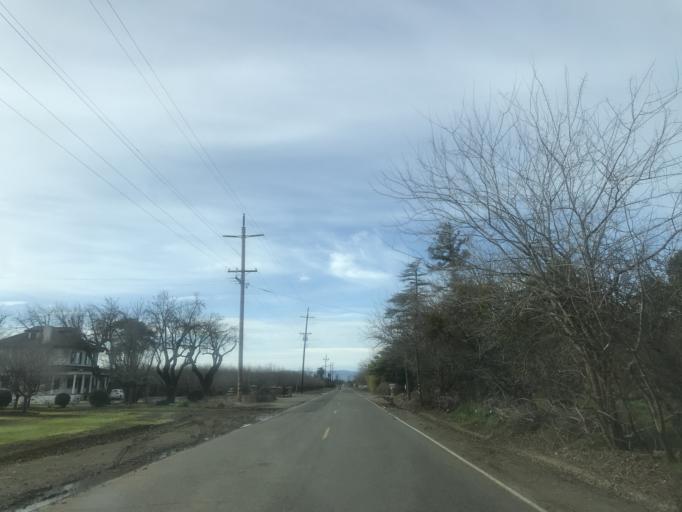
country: US
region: California
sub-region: Yolo County
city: Woodland
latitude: 38.6634
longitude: -121.8298
